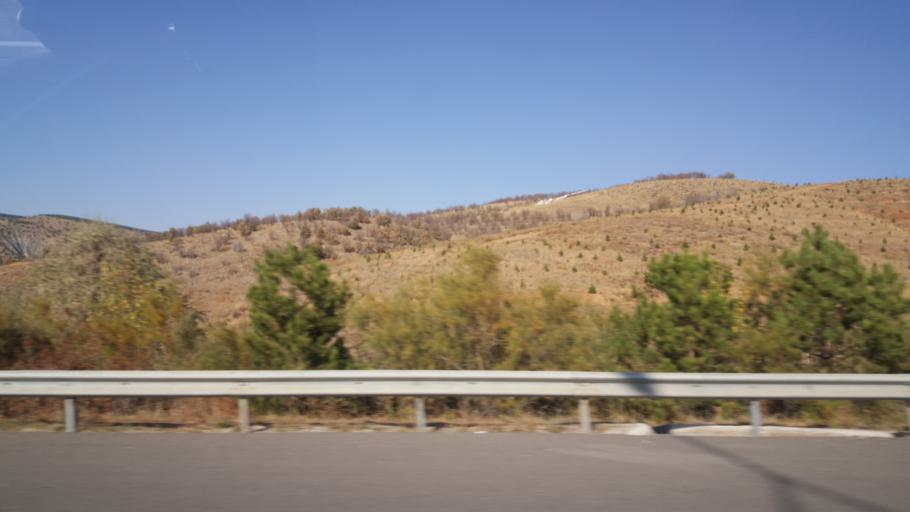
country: TR
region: Ankara
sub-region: Goelbasi
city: Golbasi
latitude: 39.8126
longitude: 32.8231
